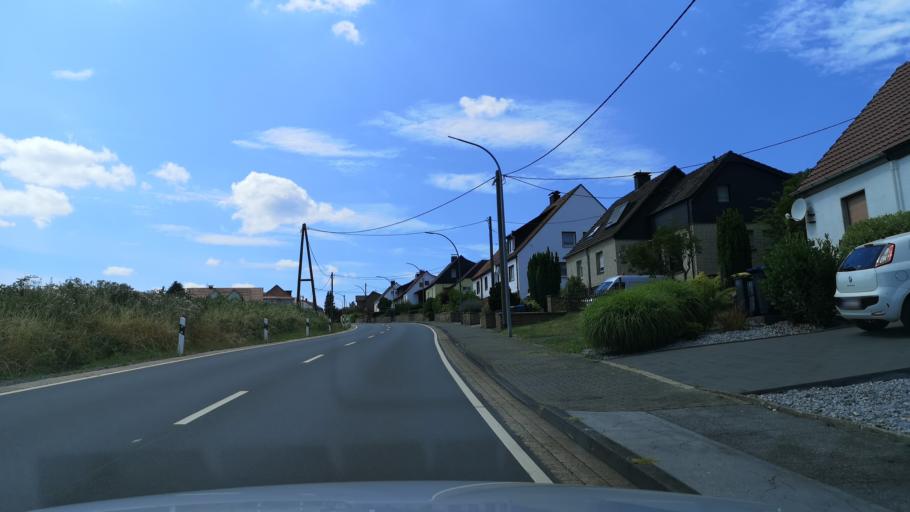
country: DE
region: North Rhine-Westphalia
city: Hemer
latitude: 51.4019
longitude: 7.7515
